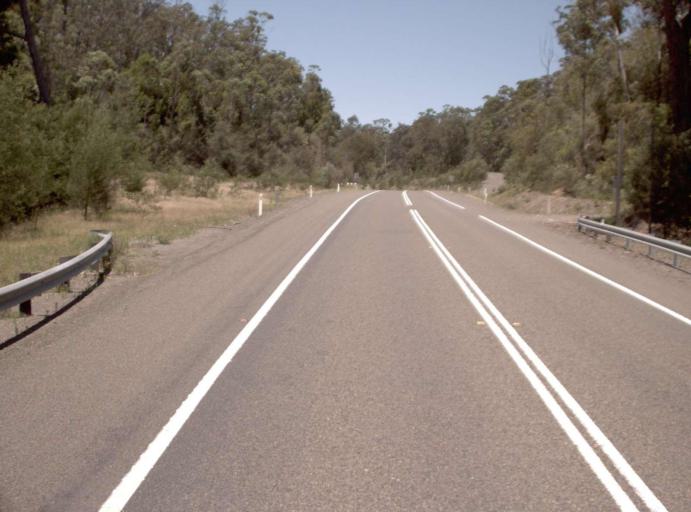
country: AU
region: Victoria
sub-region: East Gippsland
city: Lakes Entrance
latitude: -37.7313
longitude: 148.0989
